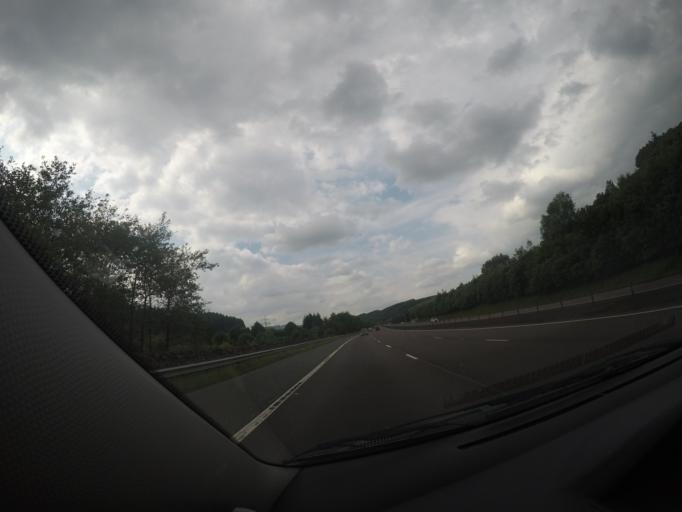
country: GB
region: Scotland
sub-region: Dumfries and Galloway
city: Moffat
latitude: 55.3319
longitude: -3.4780
